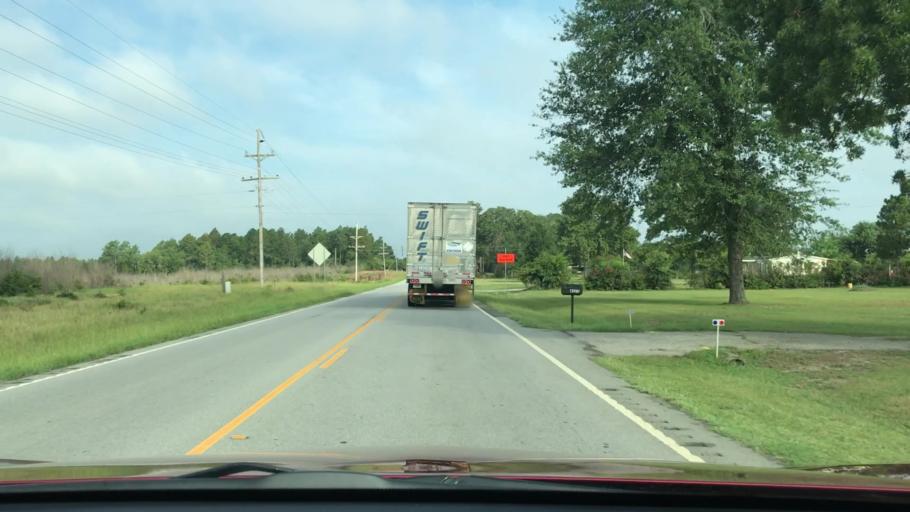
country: US
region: South Carolina
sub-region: Barnwell County
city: Williston
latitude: 33.6394
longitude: -81.3311
